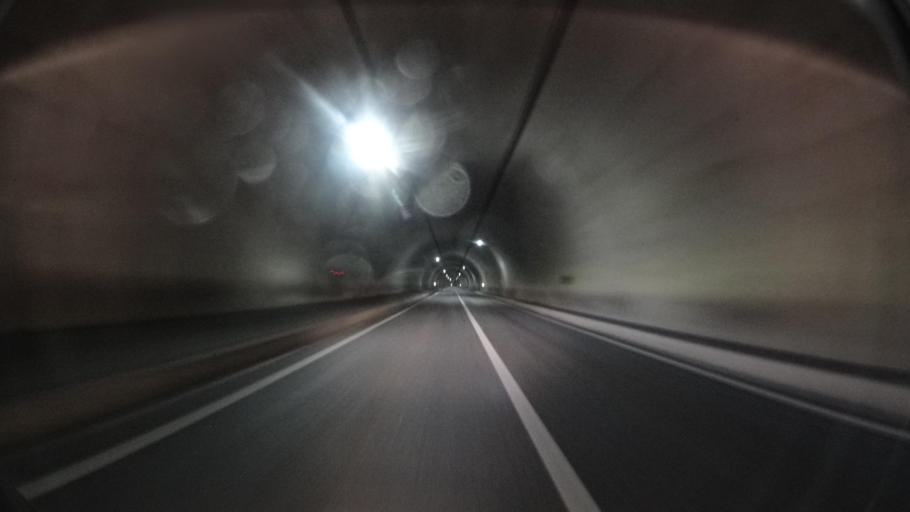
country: JP
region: Kyoto
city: Maizuru
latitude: 35.5230
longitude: 135.3476
